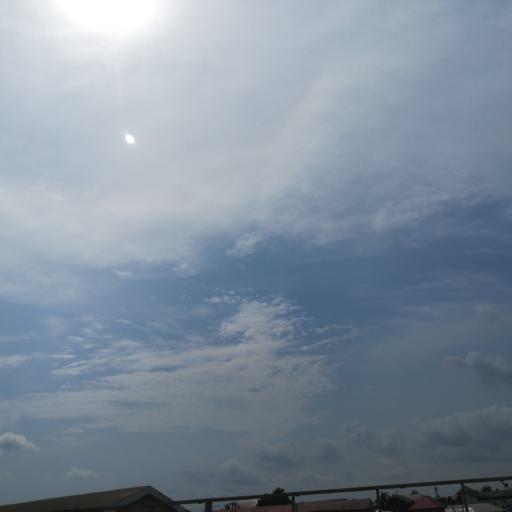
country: NG
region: Rivers
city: Port Harcourt
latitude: 4.8592
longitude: 7.0218
